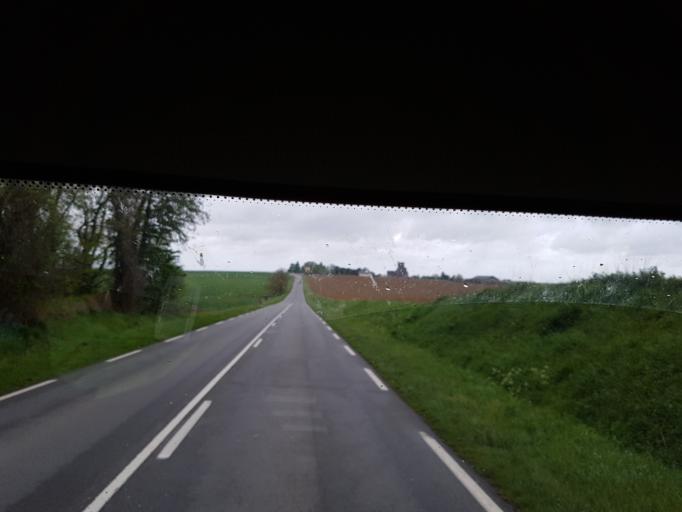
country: FR
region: Picardie
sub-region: Departement de l'Aisne
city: Crouy
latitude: 49.4389
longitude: 3.3564
